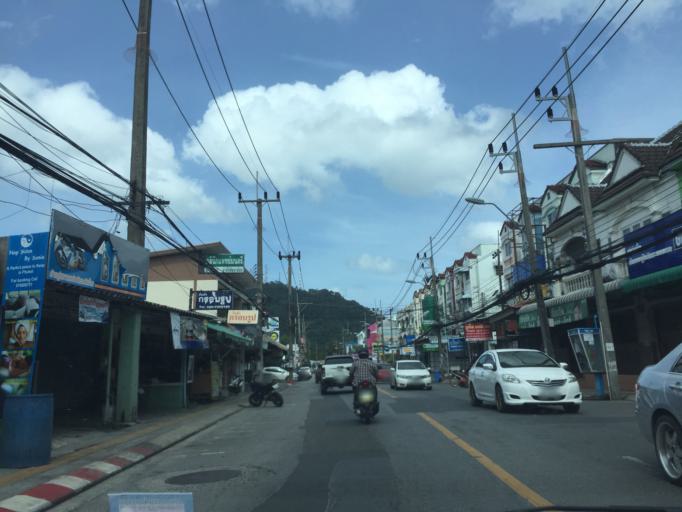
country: TH
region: Phuket
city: Wichit
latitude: 7.9025
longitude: 98.3782
